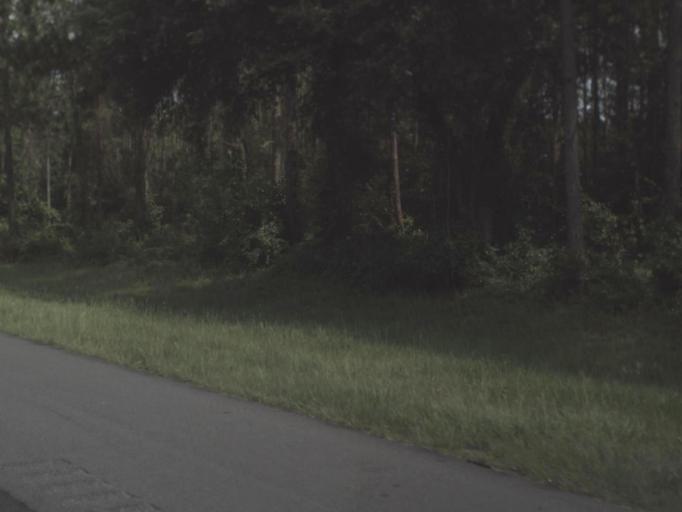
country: US
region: Georgia
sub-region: Echols County
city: Statenville
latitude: 30.6126
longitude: -83.1431
